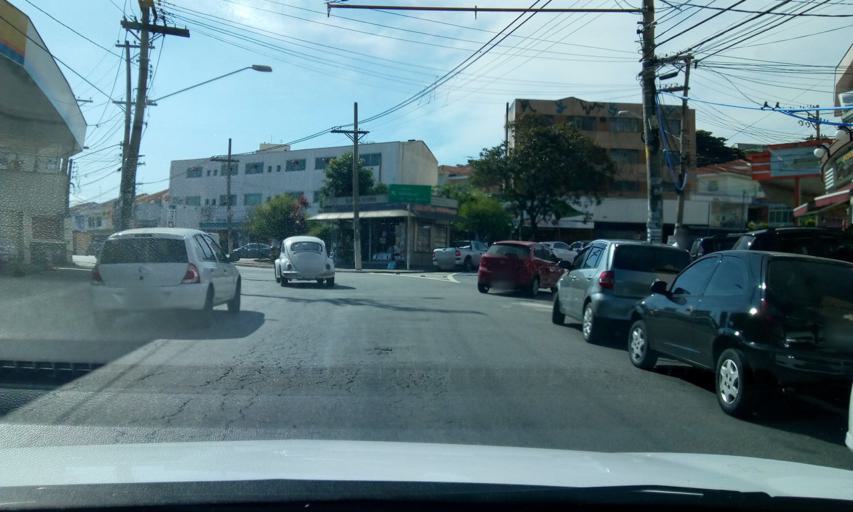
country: BR
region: Sao Paulo
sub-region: Sao Paulo
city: Sao Paulo
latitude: -23.5084
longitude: -46.6657
